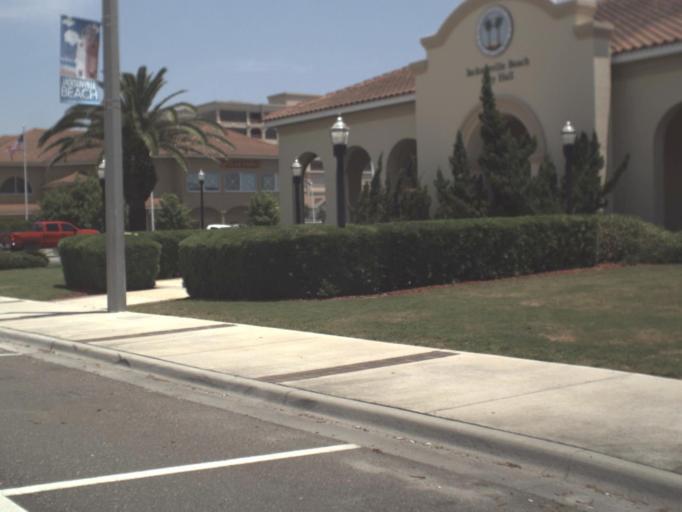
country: US
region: Florida
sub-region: Duval County
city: Jacksonville Beach
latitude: 30.2895
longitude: -81.3920
